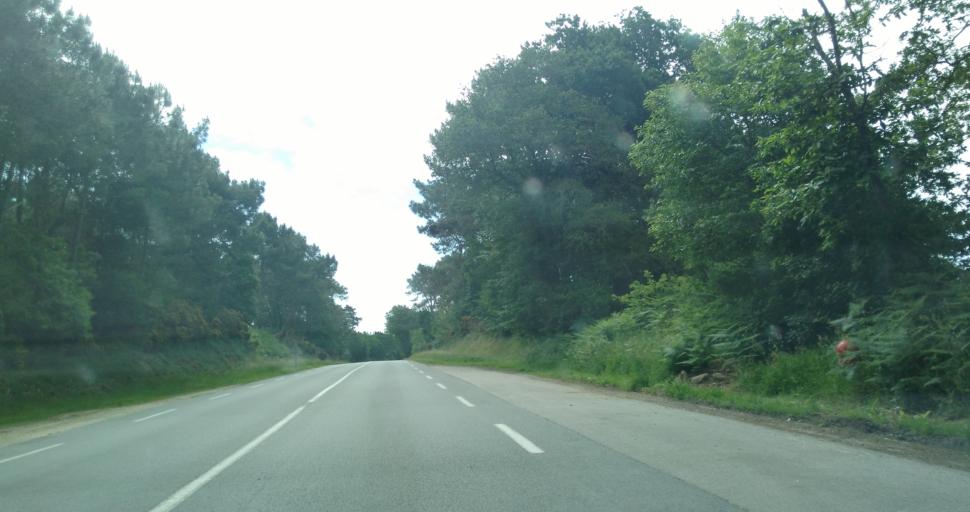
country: FR
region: Brittany
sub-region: Departement du Morbihan
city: La Trinite-sur-Mer
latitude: 47.6082
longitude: -3.0464
